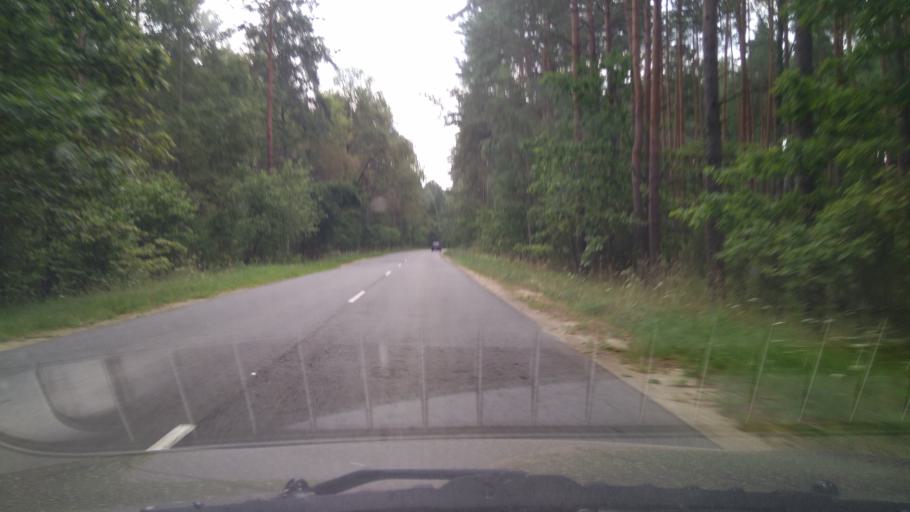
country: BY
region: Brest
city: Nyakhachava
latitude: 52.5998
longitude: 25.0970
